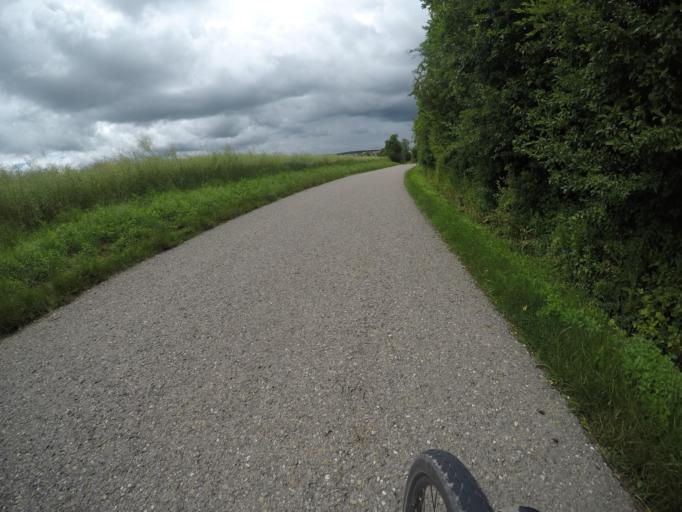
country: DE
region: Baden-Wuerttemberg
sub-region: Regierungsbezirk Stuttgart
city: Unterjettingen
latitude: 48.5720
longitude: 8.7925
